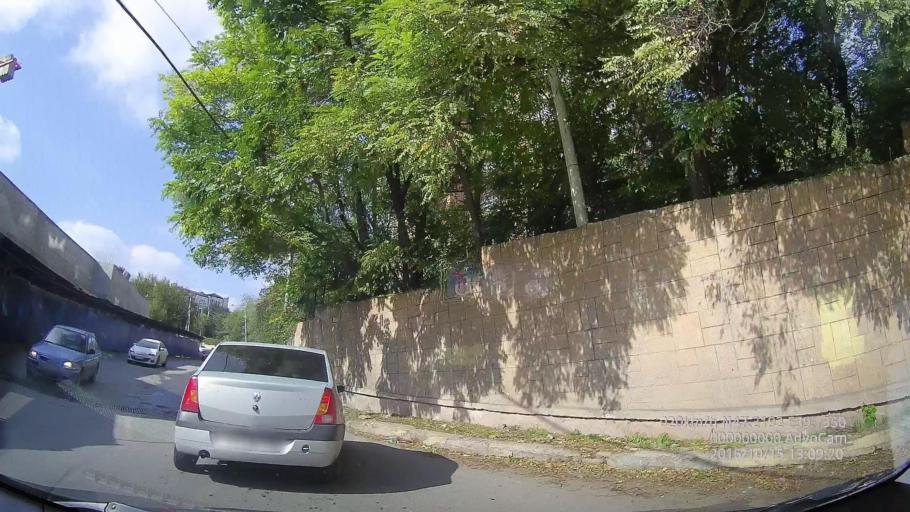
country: RU
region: Rostov
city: Rostov-na-Donu
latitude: 47.2196
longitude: 39.7337
